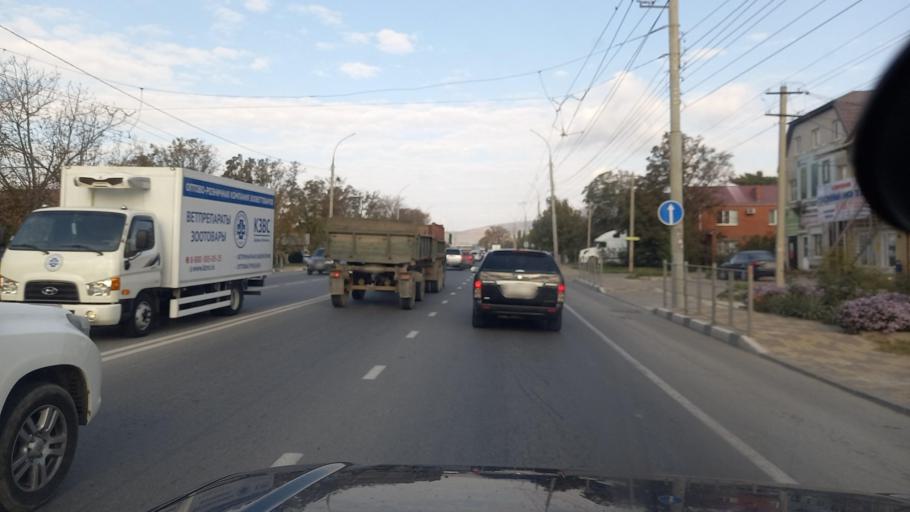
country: RU
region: Krasnodarskiy
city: Gayduk
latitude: 44.7578
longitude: 37.7241
